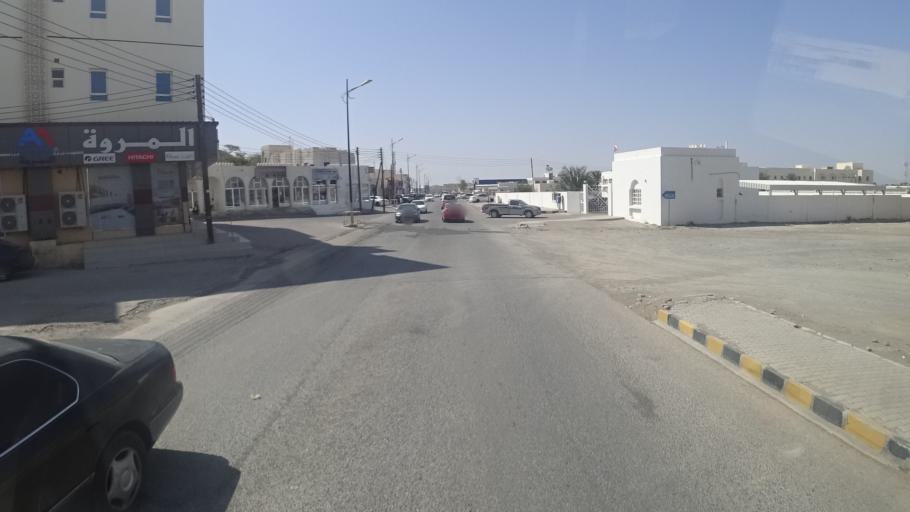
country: OM
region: Ash Sharqiyah
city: Ibra'
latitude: 22.6963
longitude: 58.5461
